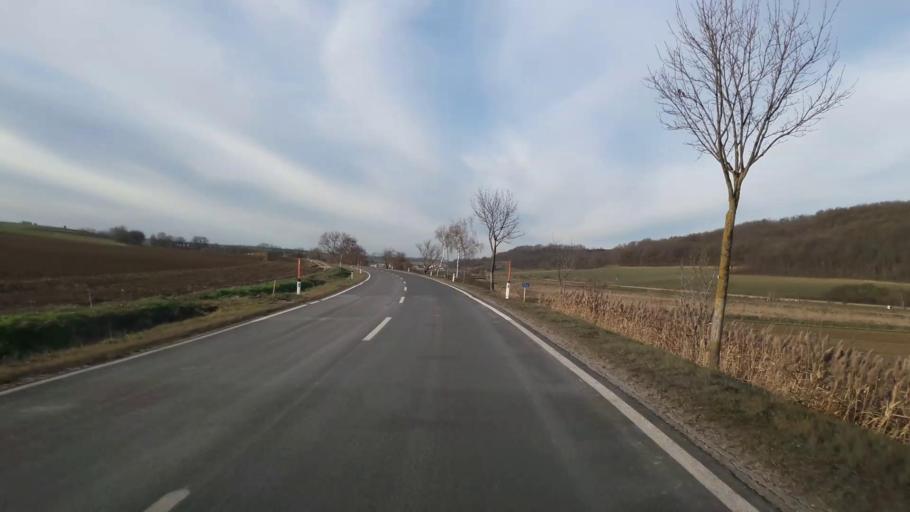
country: AT
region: Lower Austria
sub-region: Politischer Bezirk Ganserndorf
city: Gross-Schweinbarth
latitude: 48.4245
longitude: 16.6244
